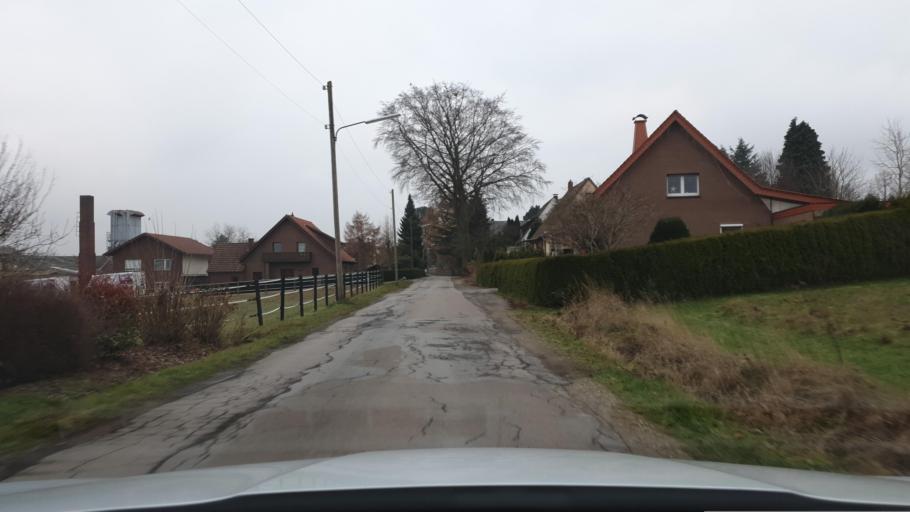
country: DE
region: North Rhine-Westphalia
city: Bad Oeynhausen
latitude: 52.1699
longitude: 8.8057
